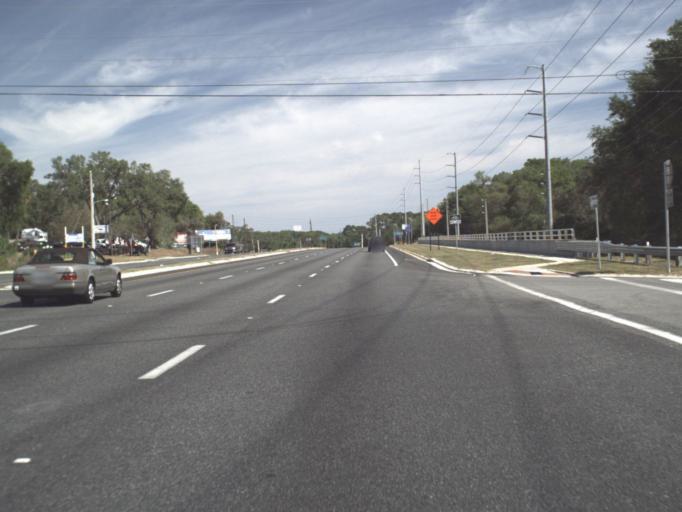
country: US
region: Florida
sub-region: Lake County
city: Fruitland Park
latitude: 28.8576
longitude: -81.9033
